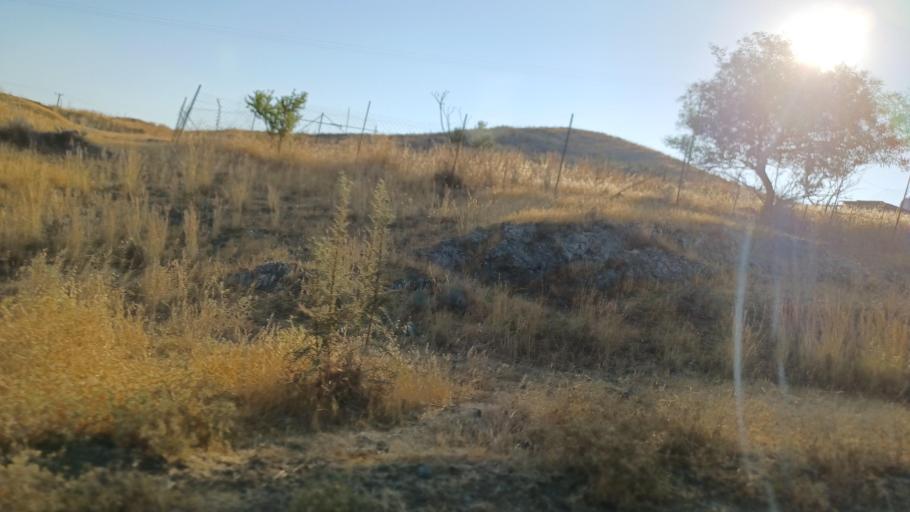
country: CY
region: Larnaka
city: Troulloi
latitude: 35.0118
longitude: 33.6009
